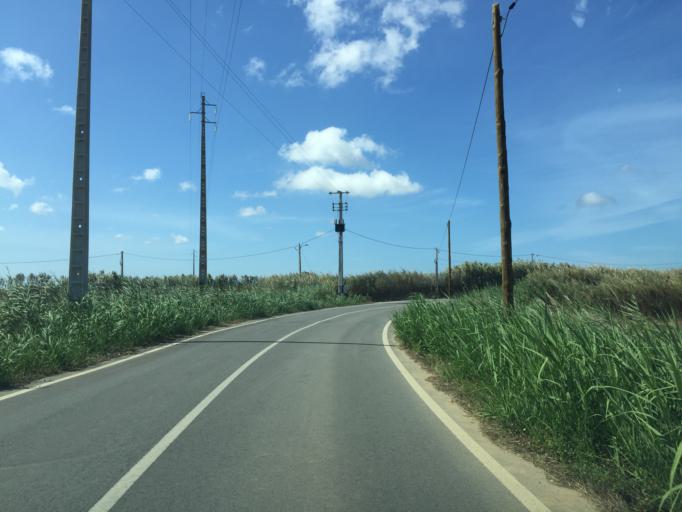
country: PT
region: Lisbon
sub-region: Lourinha
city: Lourinha
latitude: 39.2699
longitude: -9.2984
